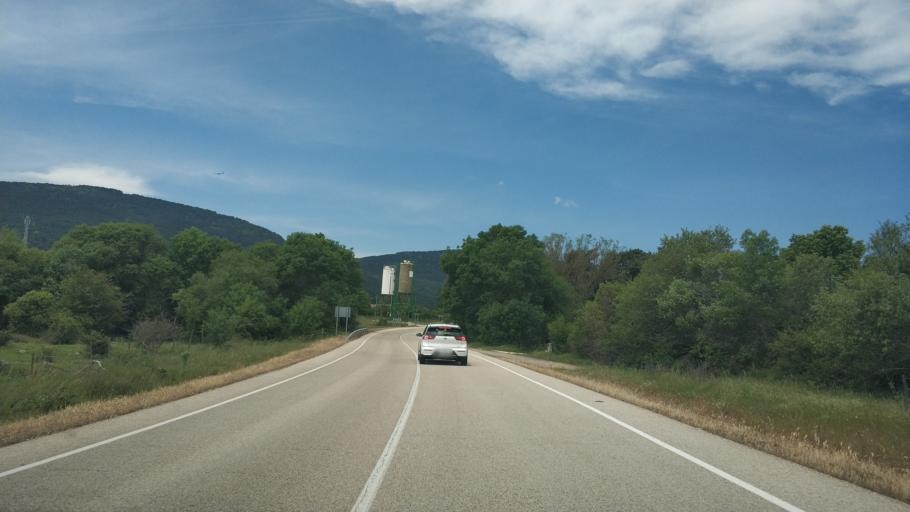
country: ES
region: Castille and Leon
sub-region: Provincia de Soria
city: Vinuesa
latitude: 41.9090
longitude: -2.7490
